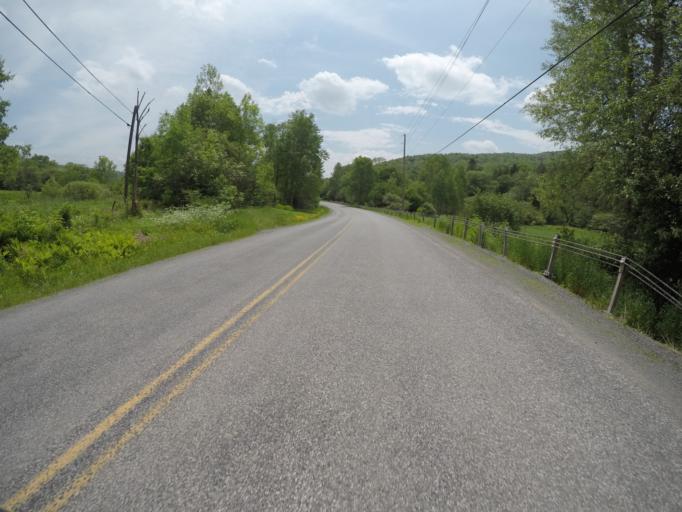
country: US
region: New York
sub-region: Delaware County
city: Stamford
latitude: 42.2013
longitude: -74.6782
